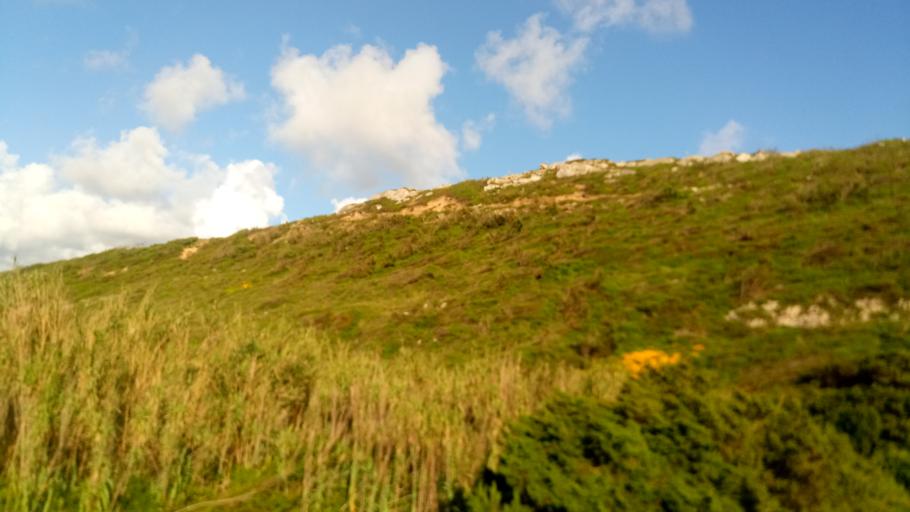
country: PT
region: Leiria
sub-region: Caldas da Rainha
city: Caldas da Rainha
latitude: 39.5072
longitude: -9.1496
